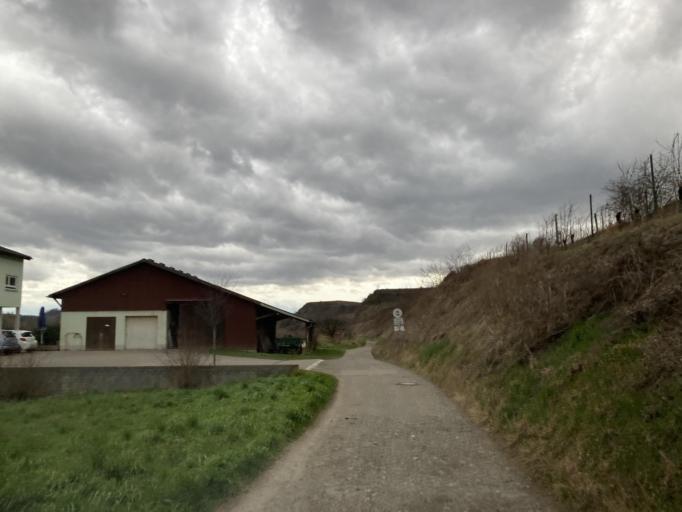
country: DE
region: Baden-Wuerttemberg
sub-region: Freiburg Region
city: Vogtsburg
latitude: 48.0960
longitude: 7.6513
